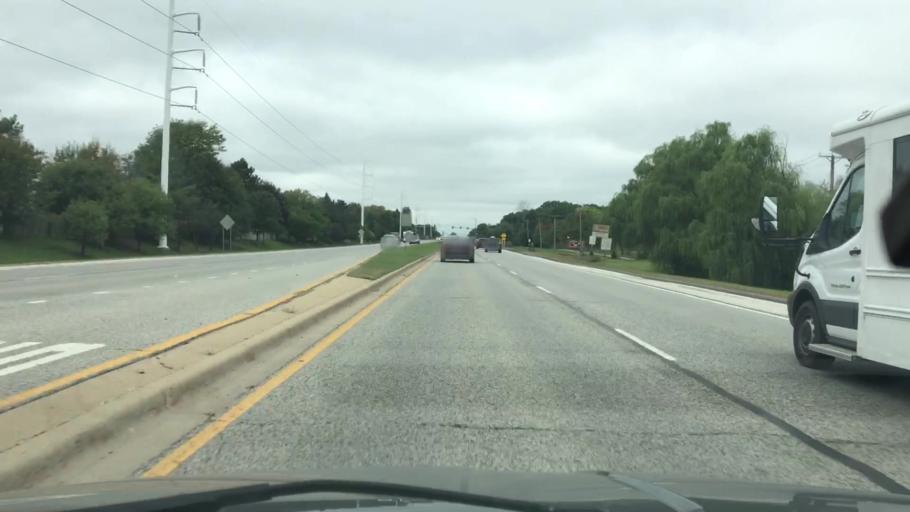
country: US
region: Illinois
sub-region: DuPage County
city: Woodridge
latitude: 41.7493
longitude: -88.0895
